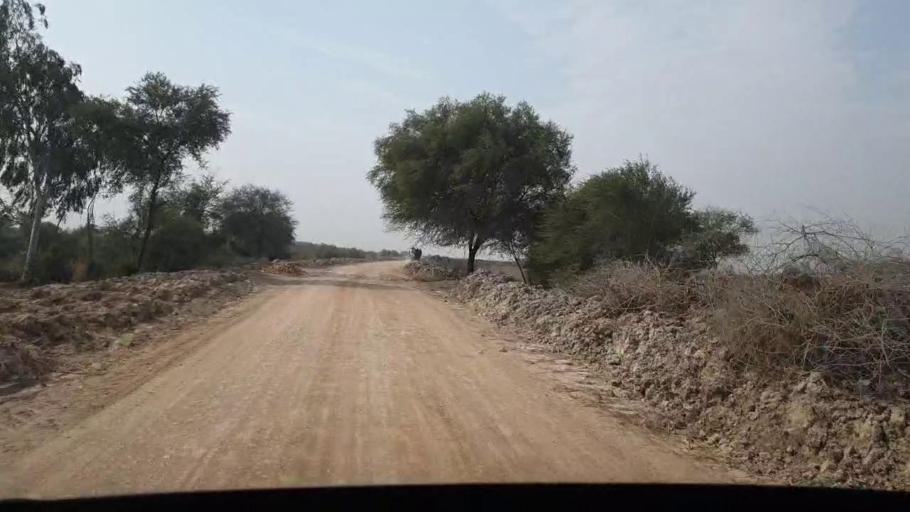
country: PK
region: Sindh
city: Chuhar Jamali
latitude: 24.3637
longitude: 67.9378
